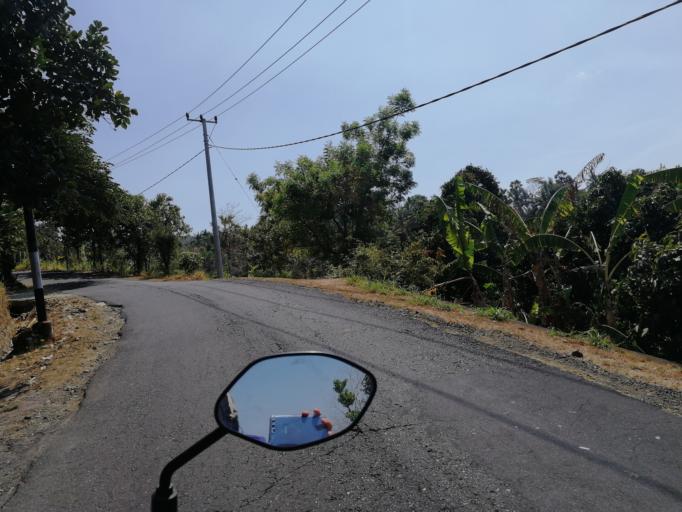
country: ID
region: Bali
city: Banjar Trunyan
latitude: -8.1301
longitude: 115.3241
